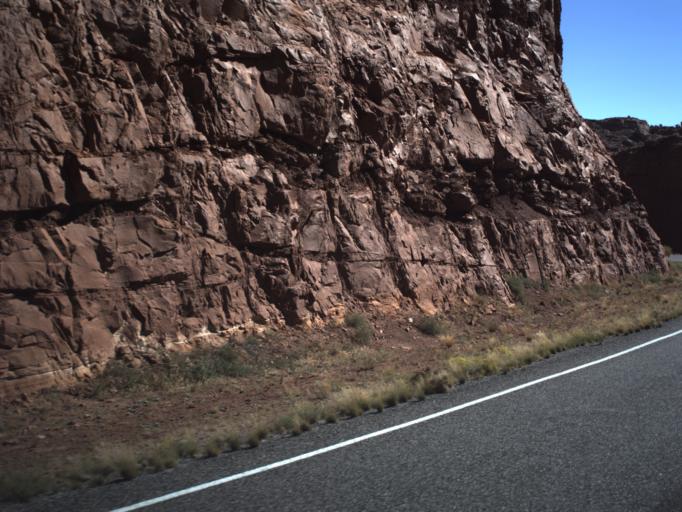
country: US
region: Utah
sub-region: San Juan County
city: Blanding
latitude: 37.9916
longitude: -110.5009
